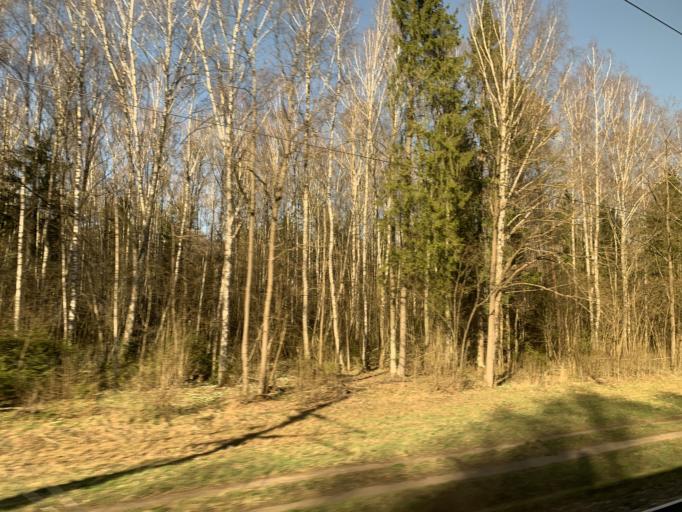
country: BY
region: Grodnenskaya
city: Smarhon'
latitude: 54.4890
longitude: 26.3034
